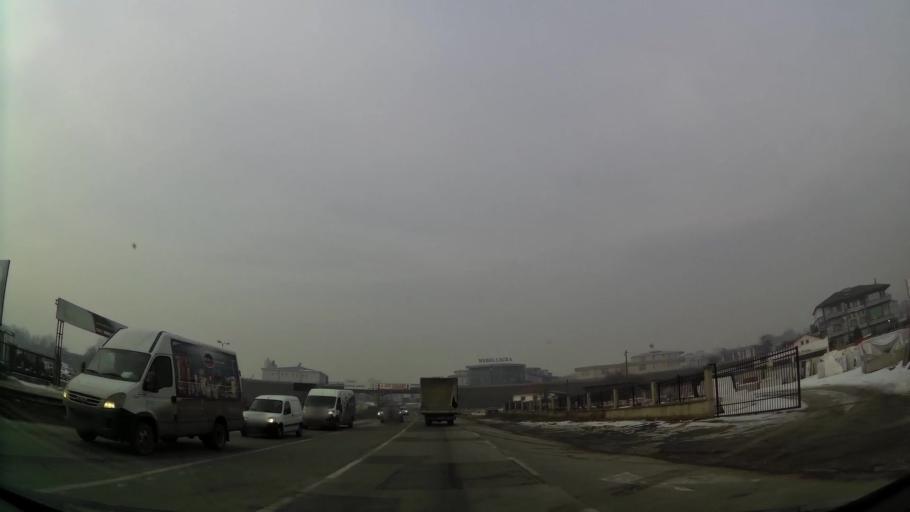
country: MK
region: Suto Orizari
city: Suto Orizare
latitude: 42.0259
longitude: 21.4088
